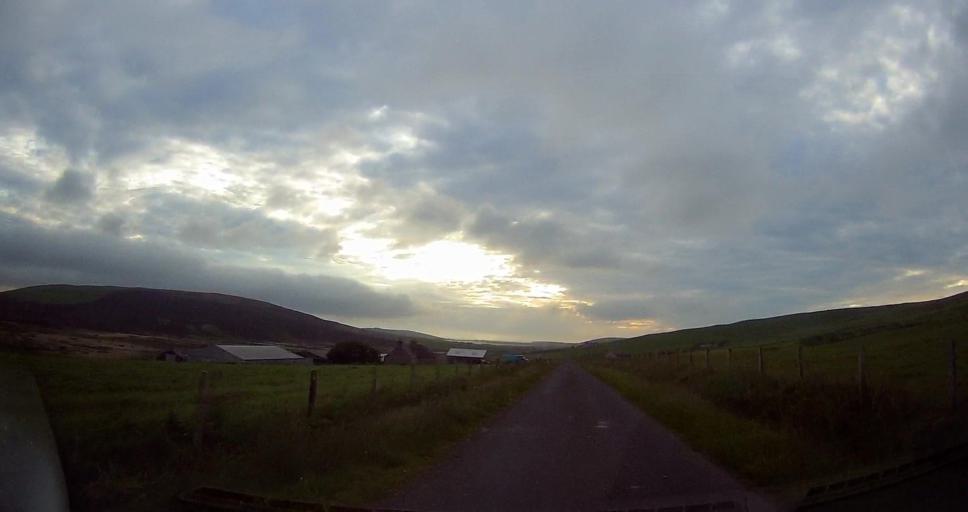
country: GB
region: Scotland
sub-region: Orkney Islands
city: Stromness
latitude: 59.0966
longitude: -3.1925
